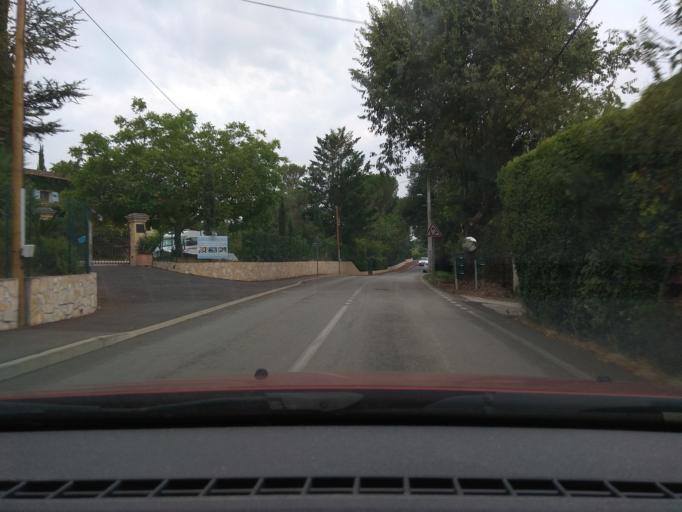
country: FR
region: Provence-Alpes-Cote d'Azur
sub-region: Departement des Alpes-Maritimes
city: Le Rouret
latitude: 43.6652
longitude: 7.0472
